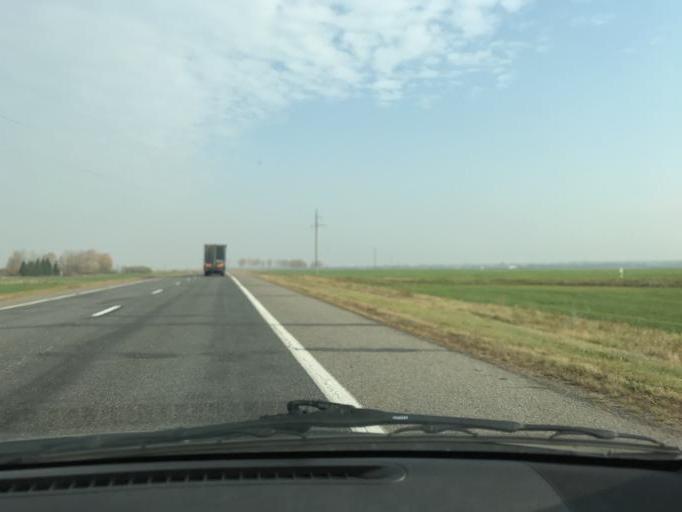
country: BY
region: Vitebsk
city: Chashniki
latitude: 55.0129
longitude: 29.1668
